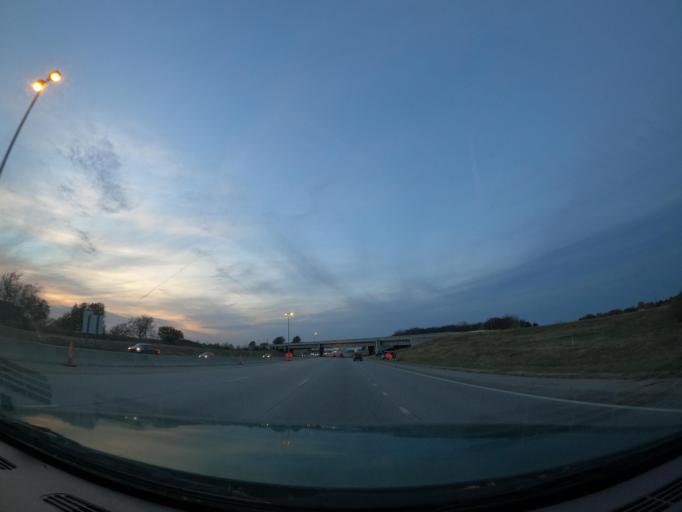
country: US
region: Oklahoma
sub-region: Tulsa County
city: Broken Arrow
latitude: 36.0748
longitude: -95.8058
